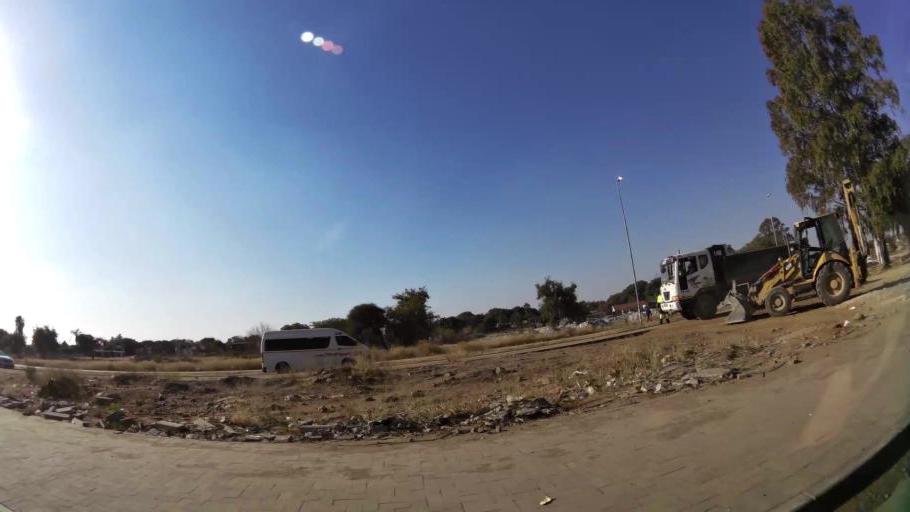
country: ZA
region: North-West
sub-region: Bojanala Platinum District Municipality
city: Rustenburg
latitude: -25.6619
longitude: 27.2315
